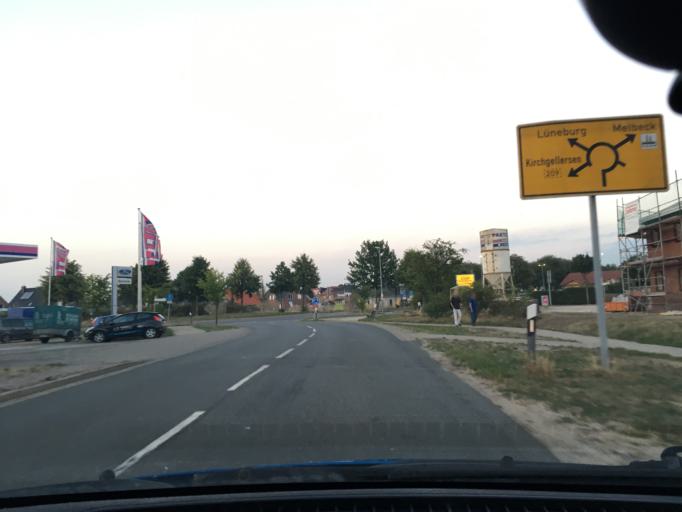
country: DE
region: Lower Saxony
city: Embsen
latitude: 53.1791
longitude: 10.3479
